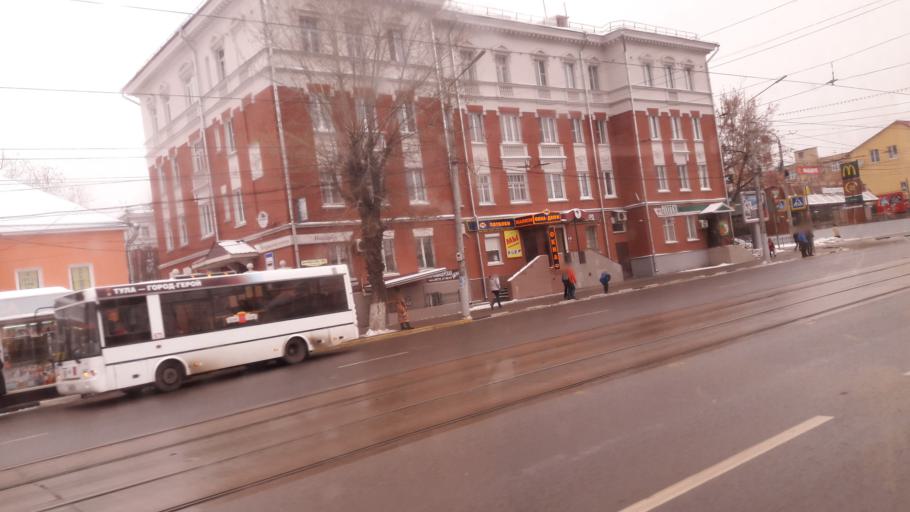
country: RU
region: Tula
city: Tula
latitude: 54.2096
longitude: 37.6210
